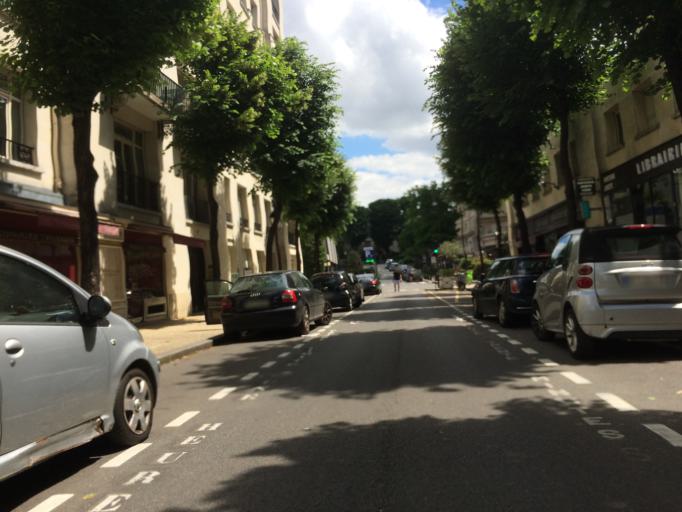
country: FR
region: Ile-de-France
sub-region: Departement des Hauts-de-Seine
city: Puteaux
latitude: 48.8769
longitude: 2.2500
